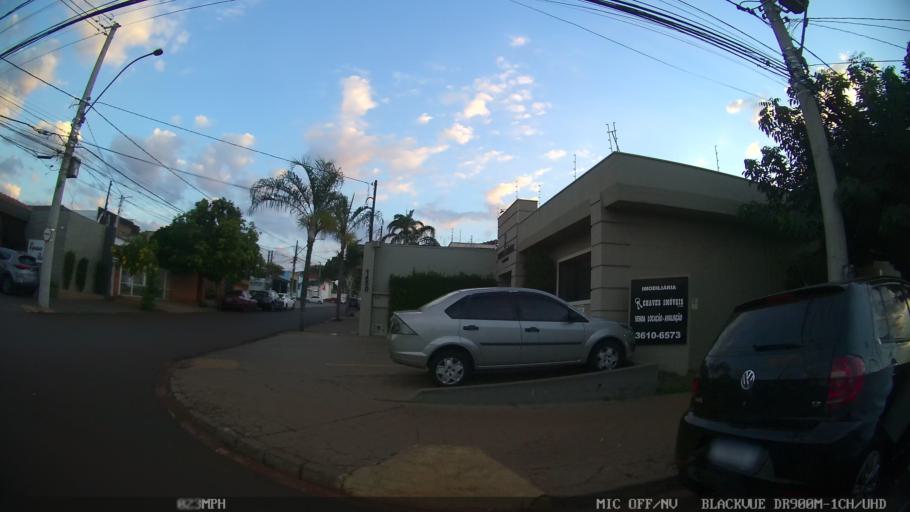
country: BR
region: Sao Paulo
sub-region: Ribeirao Preto
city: Ribeirao Preto
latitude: -21.1890
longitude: -47.8092
